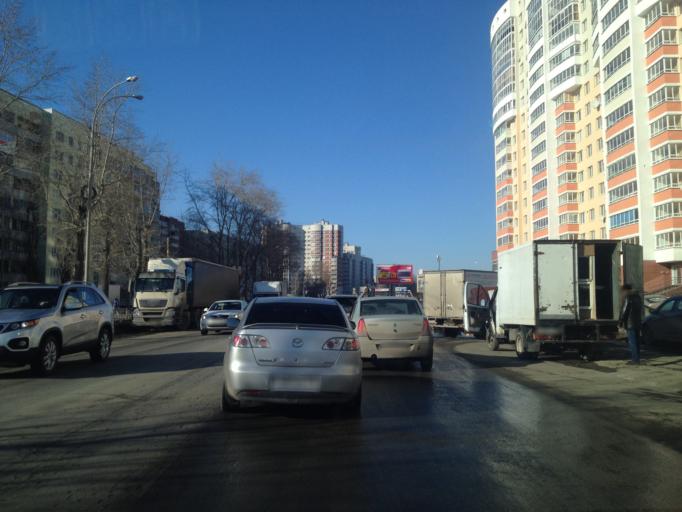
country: RU
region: Sverdlovsk
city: Yekaterinburg
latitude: 56.9060
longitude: 60.6216
